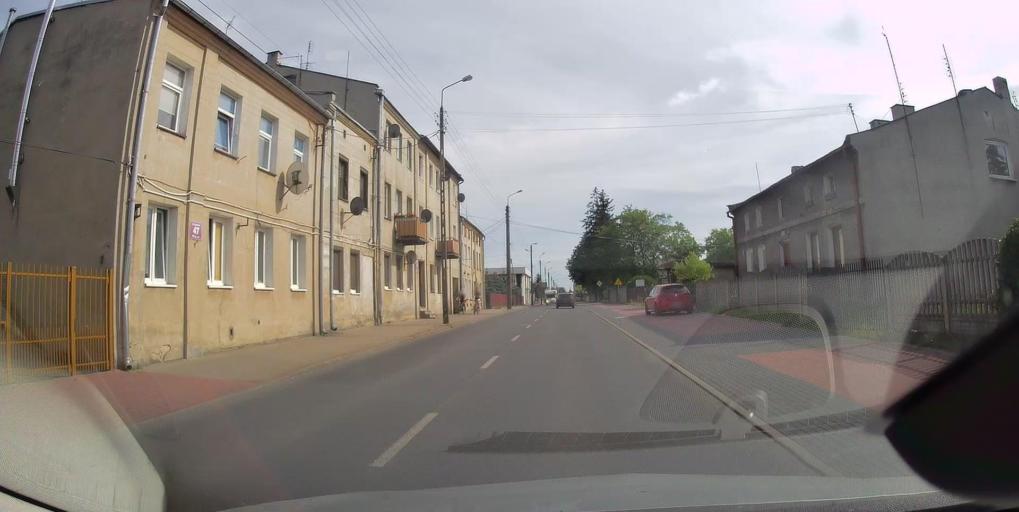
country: PL
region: Lodz Voivodeship
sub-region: Powiat tomaszowski
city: Tomaszow Mazowiecki
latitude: 51.5285
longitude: 19.9972
